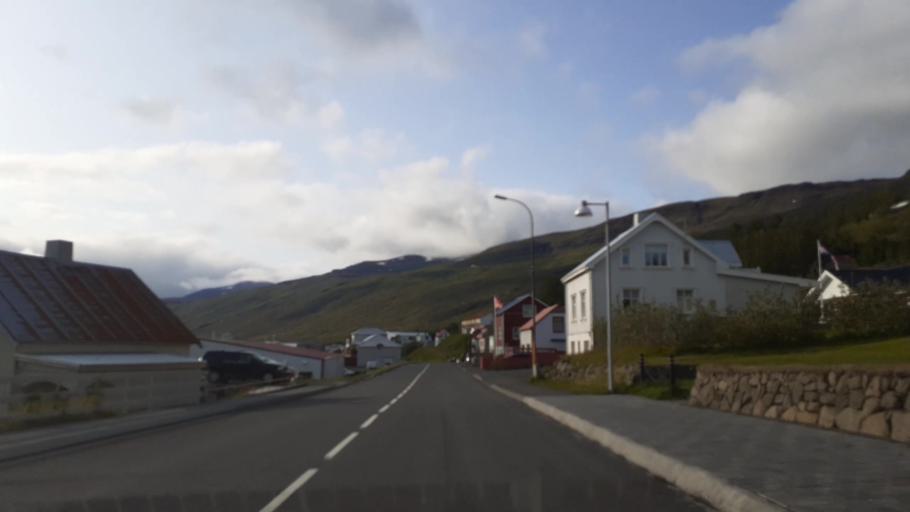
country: IS
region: East
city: Eskifjoerdur
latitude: 65.0675
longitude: -14.0056
